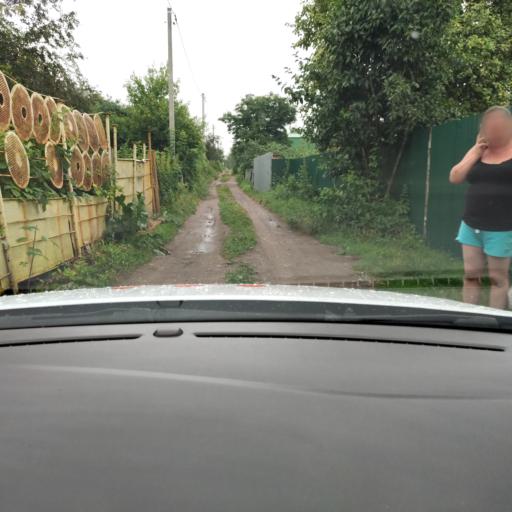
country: RU
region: Tatarstan
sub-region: Gorod Kazan'
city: Kazan
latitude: 55.8515
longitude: 49.0576
